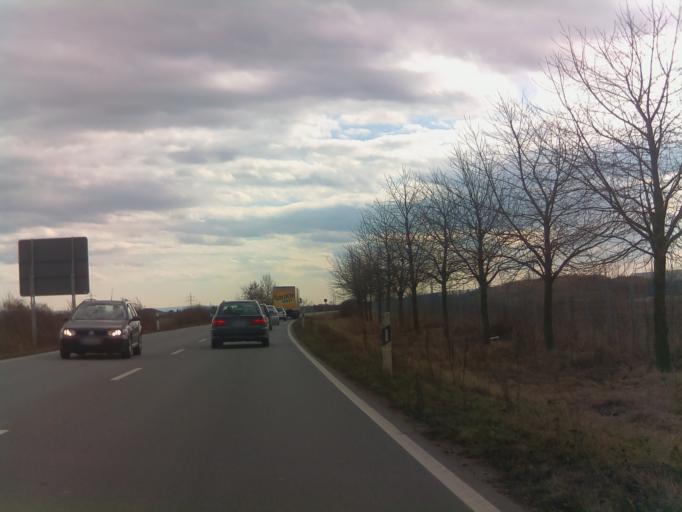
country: DE
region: Hesse
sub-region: Regierungsbezirk Darmstadt
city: Stockstadt am Rhein
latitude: 49.8119
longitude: 8.4843
